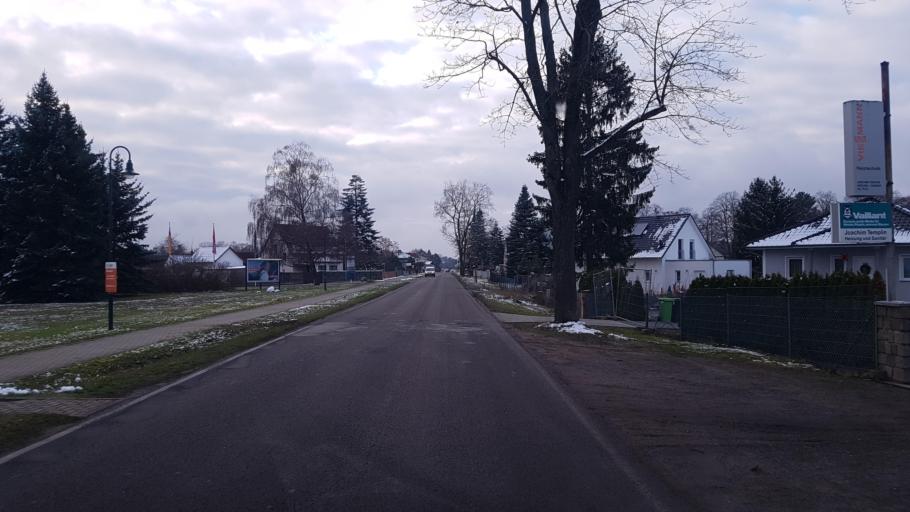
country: DE
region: Brandenburg
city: Rehfelde
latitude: 52.5087
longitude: 13.8596
